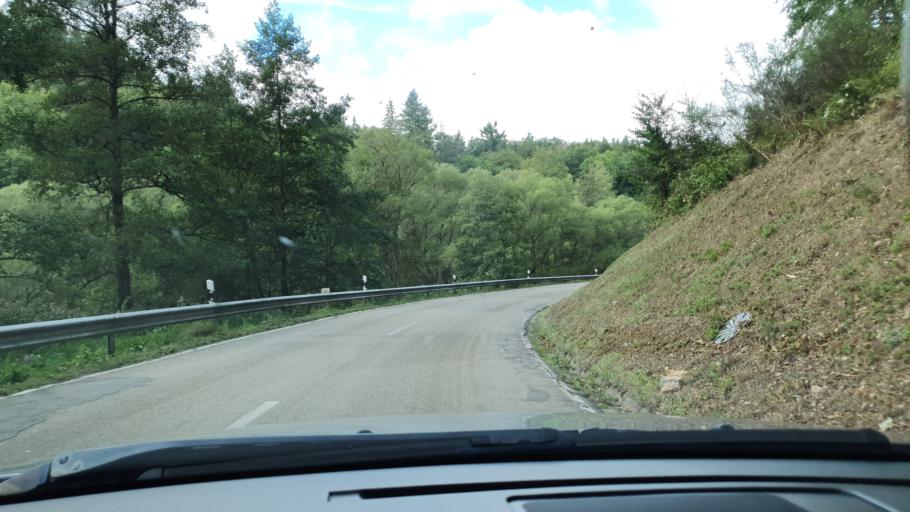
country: DE
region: Rheinland-Pfalz
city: Massweiler
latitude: 49.2619
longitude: 7.5450
